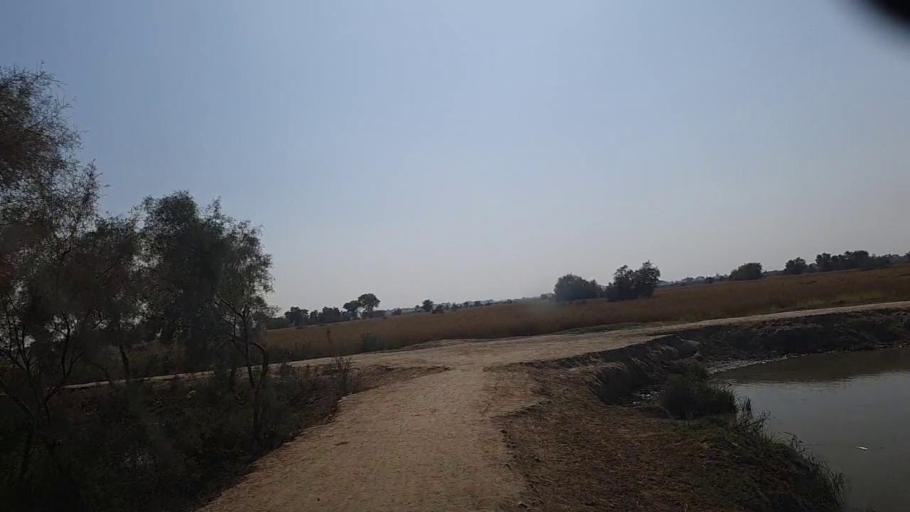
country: PK
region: Sindh
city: Thul
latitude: 28.1673
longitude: 68.7663
